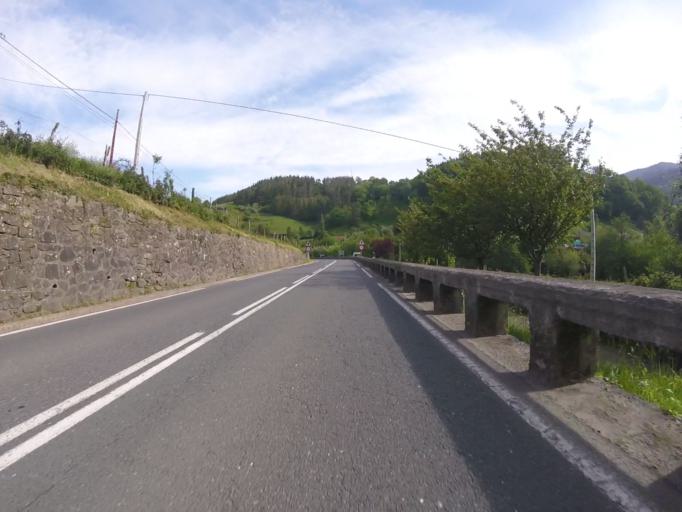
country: ES
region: Basque Country
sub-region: Provincia de Guipuzcoa
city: Urretxu
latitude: 43.1066
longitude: -2.3176
